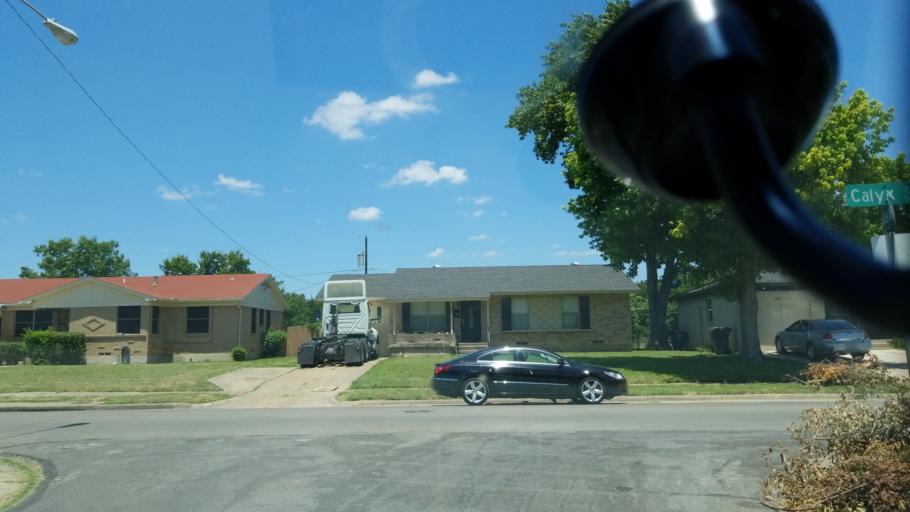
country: US
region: Texas
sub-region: Dallas County
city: Cockrell Hill
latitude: 32.6861
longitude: -96.8169
